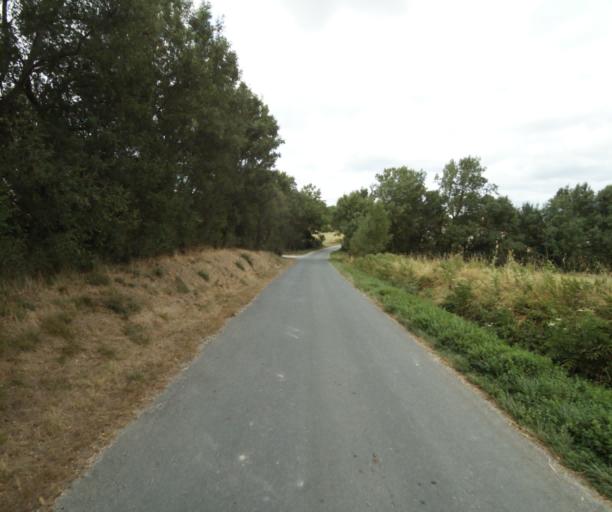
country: FR
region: Midi-Pyrenees
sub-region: Departement du Tarn
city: Soreze
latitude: 43.4682
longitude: 2.0572
